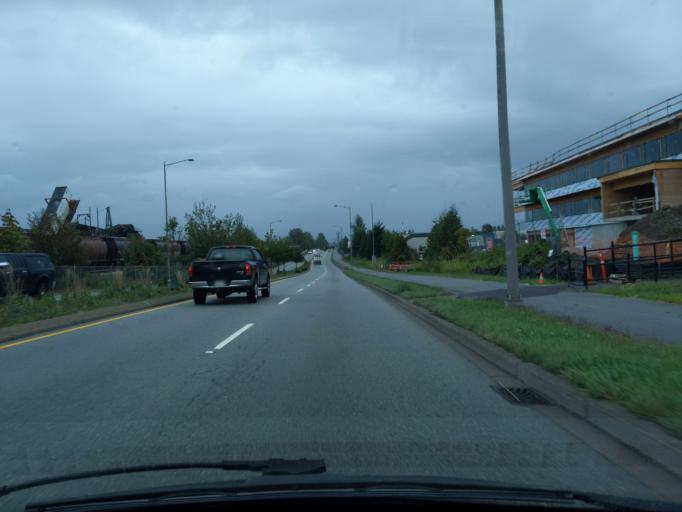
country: CA
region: British Columbia
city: Pitt Meadows
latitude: 49.1805
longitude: -122.7079
